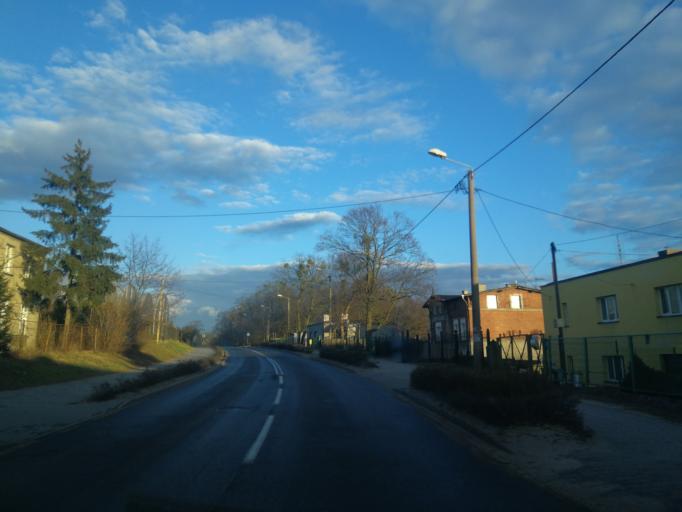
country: PL
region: Kujawsko-Pomorskie
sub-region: Powiat torunski
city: Chelmza
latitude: 53.1892
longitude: 18.6180
